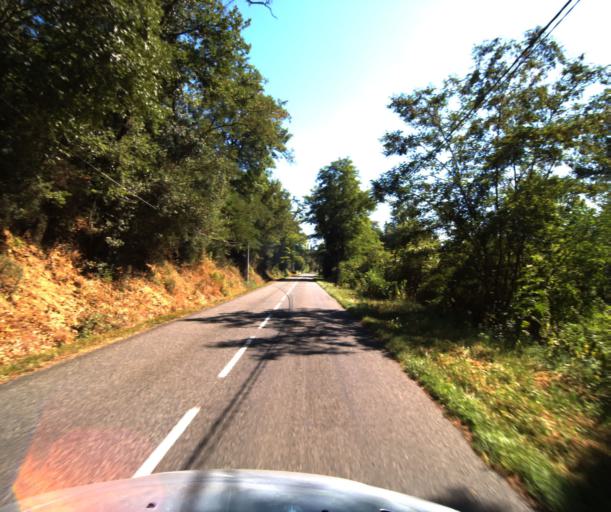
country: FR
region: Midi-Pyrenees
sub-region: Departement de la Haute-Garonne
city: Eaunes
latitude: 43.4411
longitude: 1.3282
